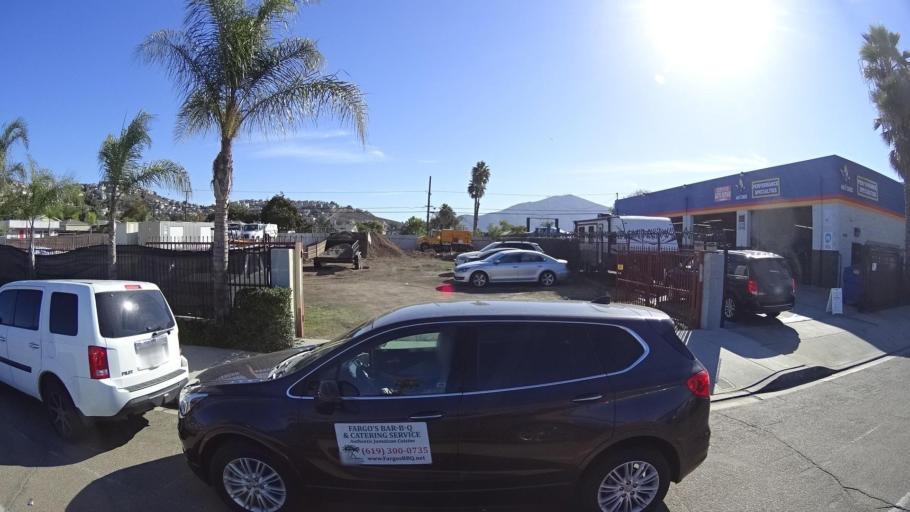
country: US
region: California
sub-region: San Diego County
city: La Presa
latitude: 32.7130
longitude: -116.9974
